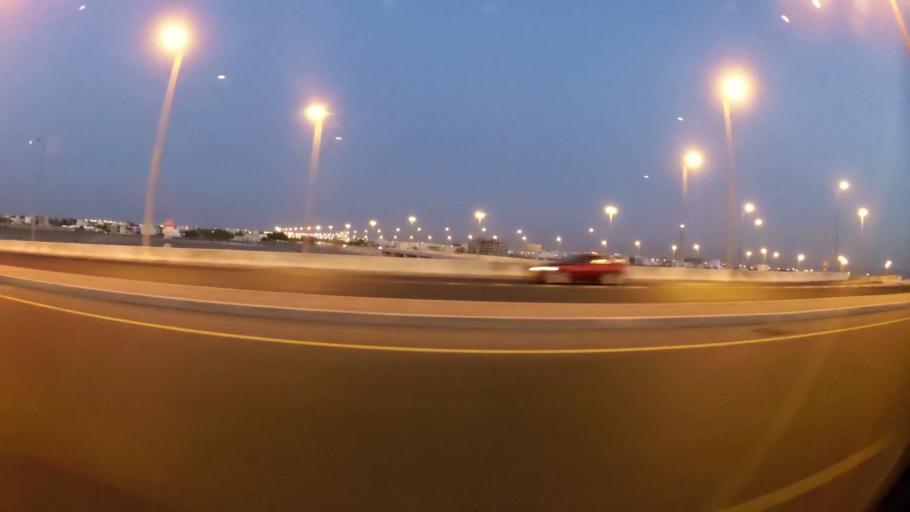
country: OM
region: Muhafazat Masqat
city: As Sib al Jadidah
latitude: 23.6599
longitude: 58.1885
